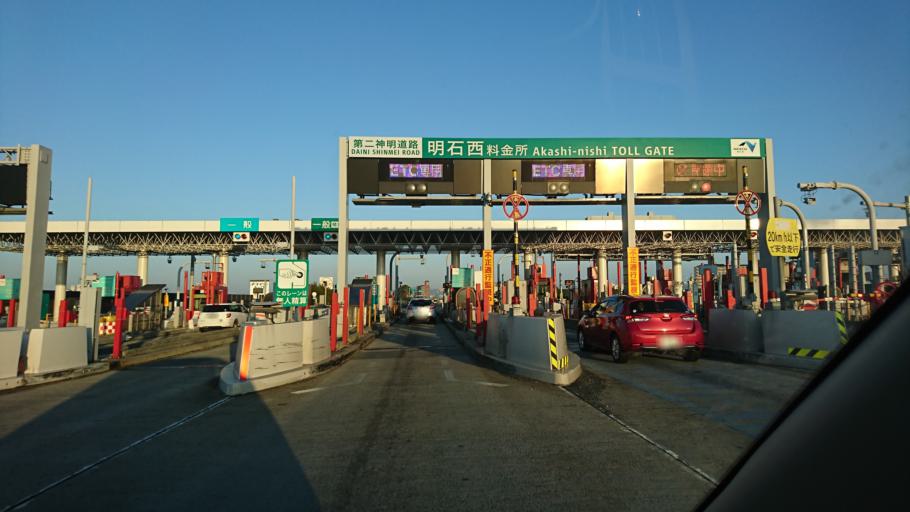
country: JP
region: Hyogo
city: Kakogawacho-honmachi
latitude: 34.7195
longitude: 134.8993
